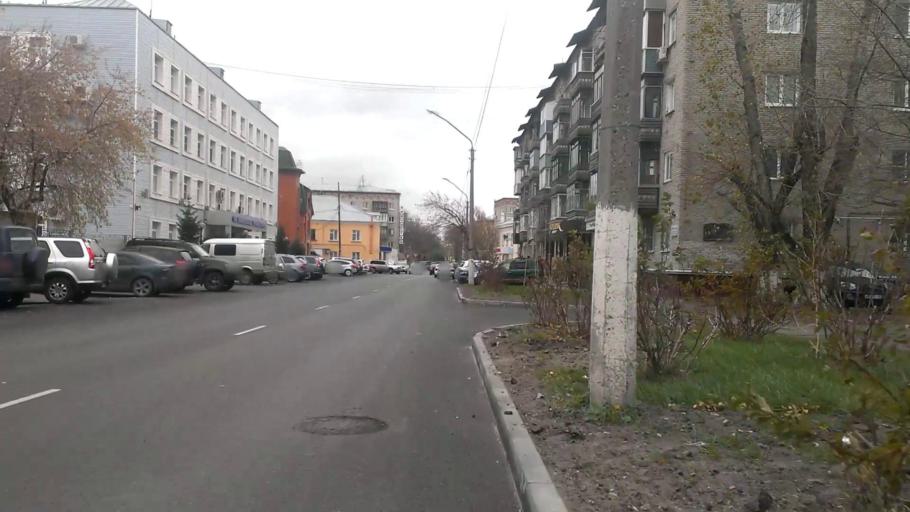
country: RU
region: Altai Krai
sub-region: Gorod Barnaulskiy
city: Barnaul
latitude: 53.3522
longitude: 83.7685
